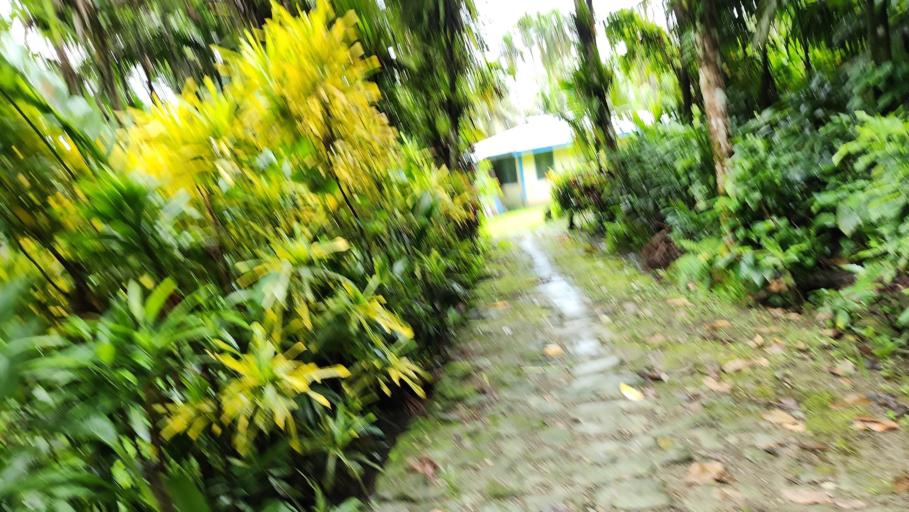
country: FM
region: Yap
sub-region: Weloy Municipality
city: Colonia
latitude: 9.5193
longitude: 138.1185
